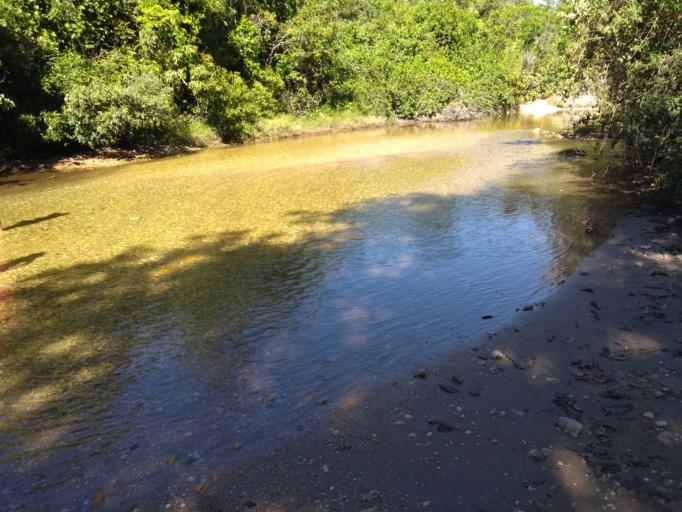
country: BR
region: Goias
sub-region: Cavalcante
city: Cavalcante
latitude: -13.8117
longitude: -47.4346
